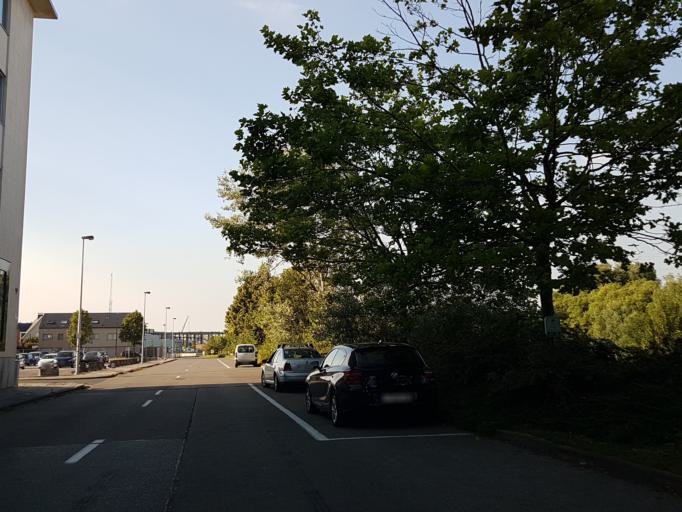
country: BE
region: Flanders
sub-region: Provincie Oost-Vlaanderen
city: Aalst
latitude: 50.9544
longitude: 4.0370
